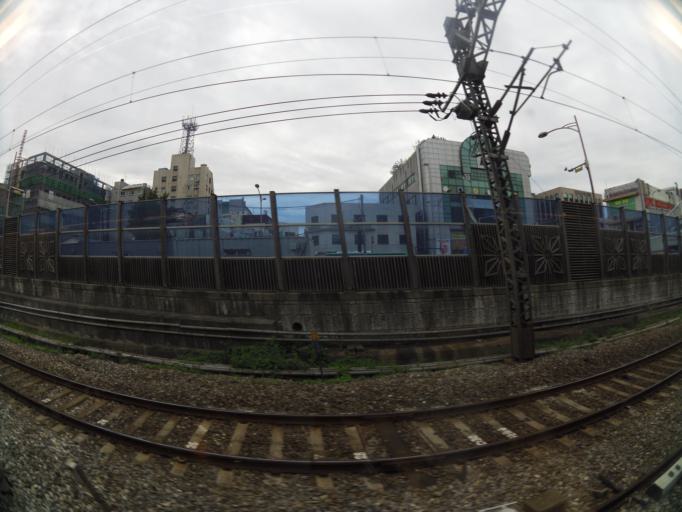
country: KR
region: Gyeonggi-do
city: Anyang-si
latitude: 37.3988
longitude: 126.9250
